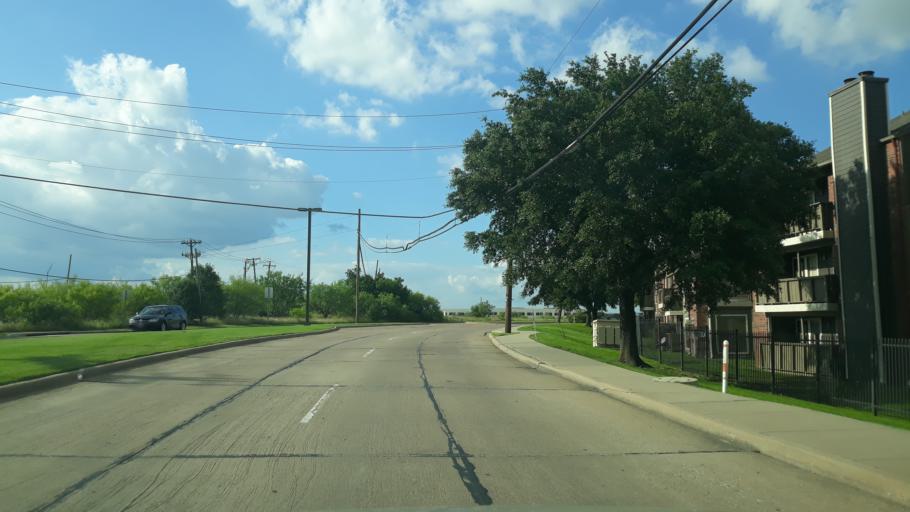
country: US
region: Texas
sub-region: Dallas County
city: Irving
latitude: 32.8590
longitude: -97.0079
